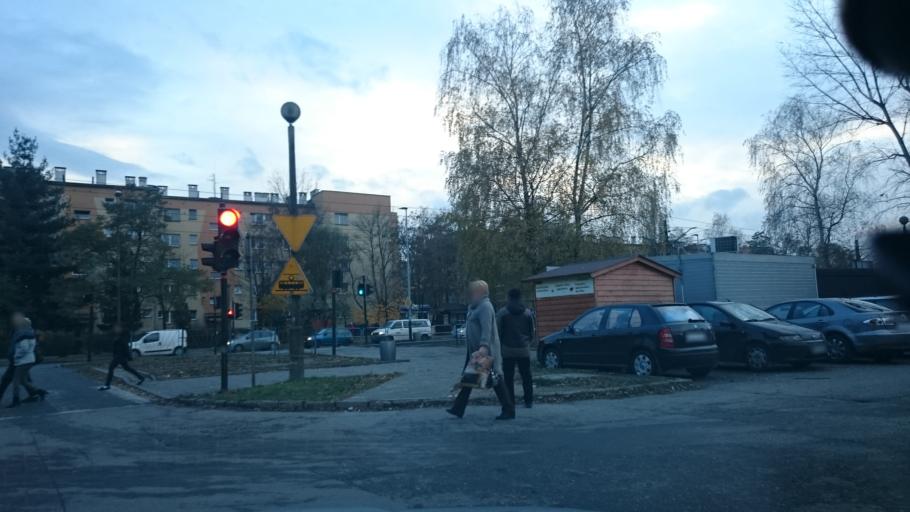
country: PL
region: Lesser Poland Voivodeship
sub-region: Powiat wielicki
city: Czarnochowice
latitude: 50.0167
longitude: 20.0077
